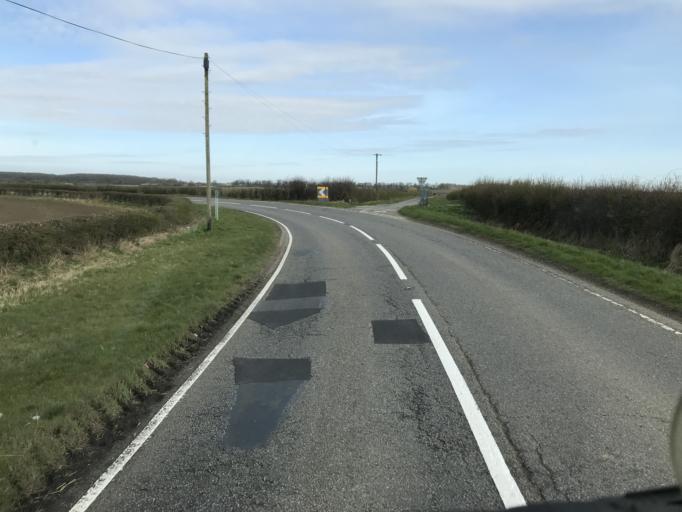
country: GB
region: England
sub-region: Lincolnshire
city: Market Rasen
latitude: 53.3946
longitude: -0.4060
